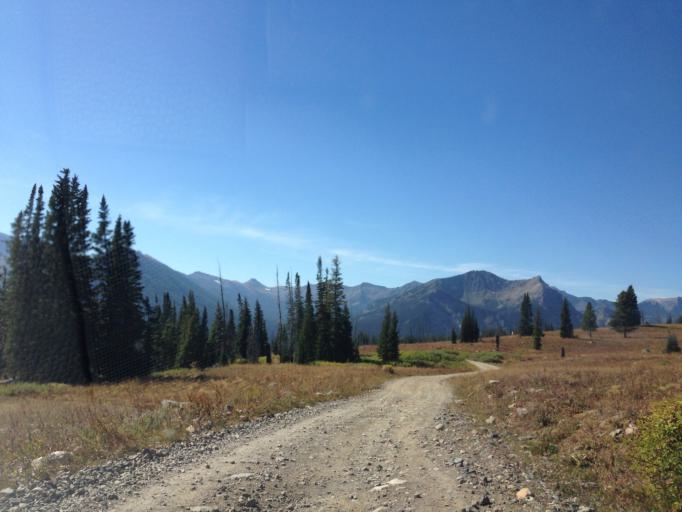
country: US
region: Montana
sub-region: Stillwater County
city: Absarokee
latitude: 45.0413
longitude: -109.9127
